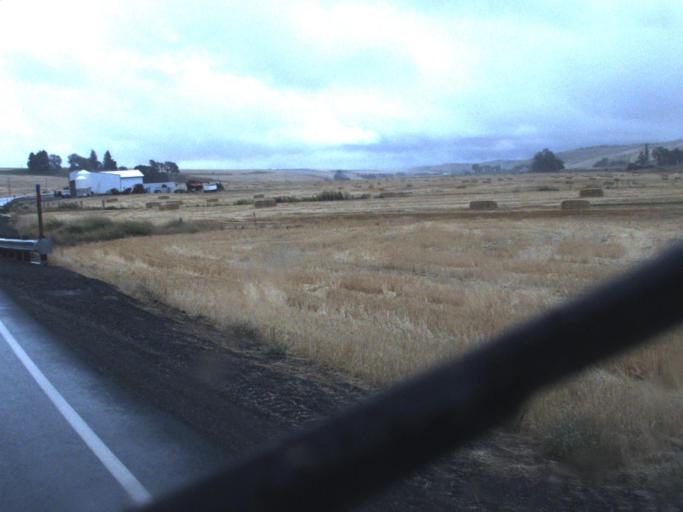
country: US
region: Washington
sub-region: Whitman County
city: Colfax
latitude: 47.0853
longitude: -117.5470
